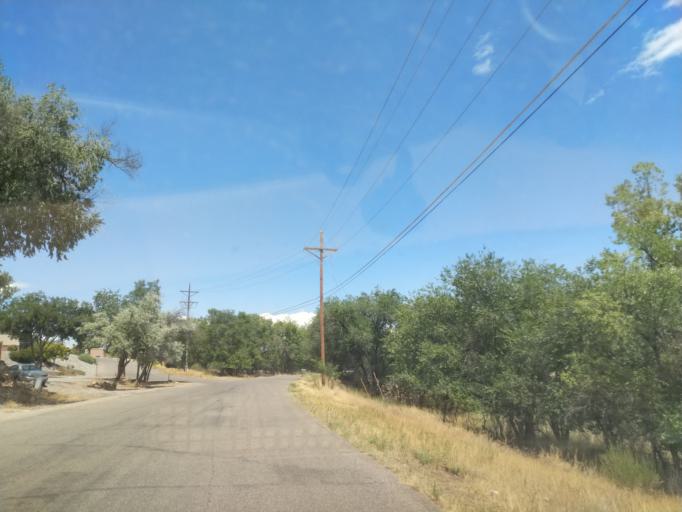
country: US
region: Colorado
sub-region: Mesa County
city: Redlands
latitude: 39.0780
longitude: -108.6366
